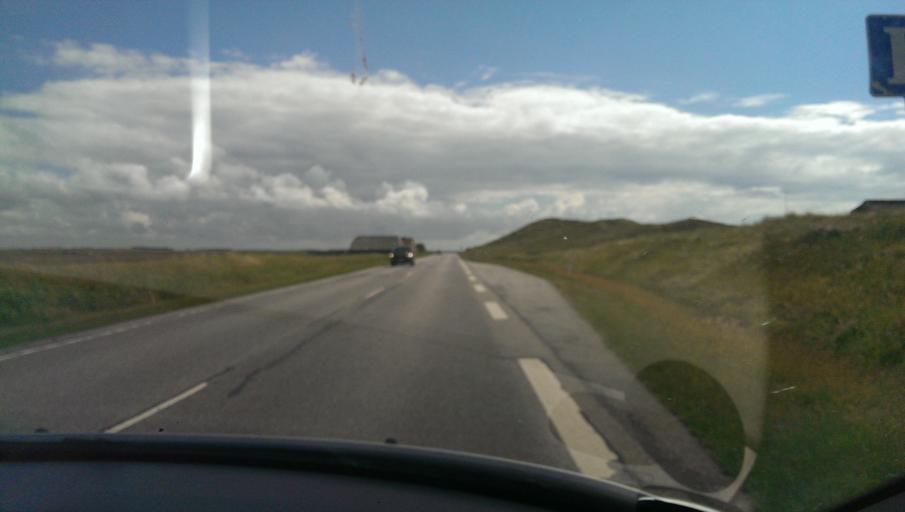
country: DK
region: Central Jutland
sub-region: Ringkobing-Skjern Kommune
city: Ringkobing
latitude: 56.2336
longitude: 8.1390
